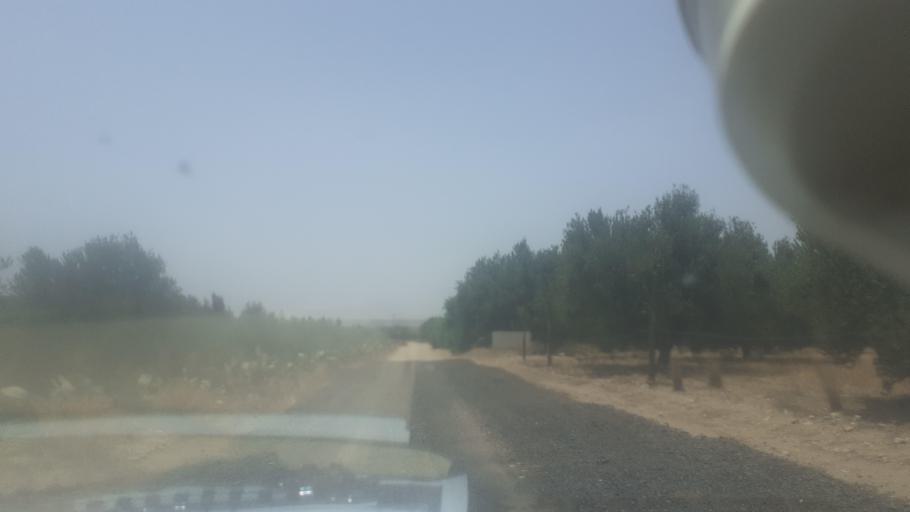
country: TN
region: Al Qasrayn
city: Kasserine
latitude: 35.2189
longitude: 8.8816
